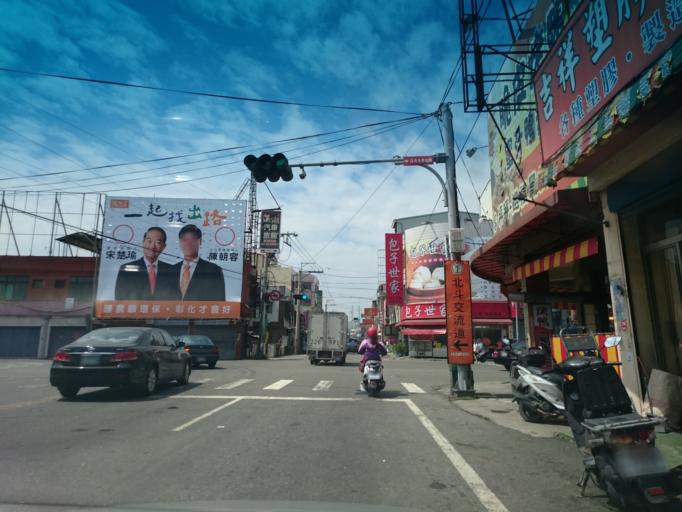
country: TW
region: Taiwan
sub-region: Changhua
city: Chang-hua
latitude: 23.9577
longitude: 120.4831
